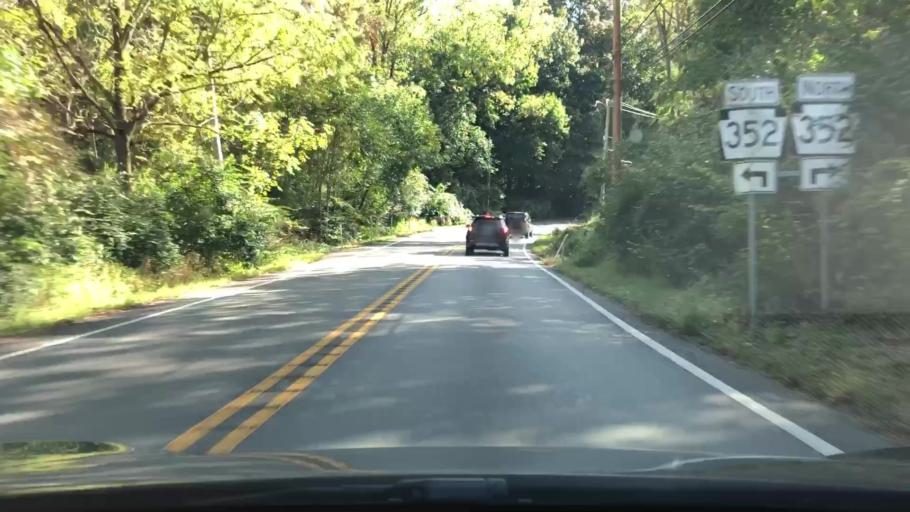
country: US
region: Pennsylvania
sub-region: Delaware County
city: Chester Heights
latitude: 39.9526
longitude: -75.5087
